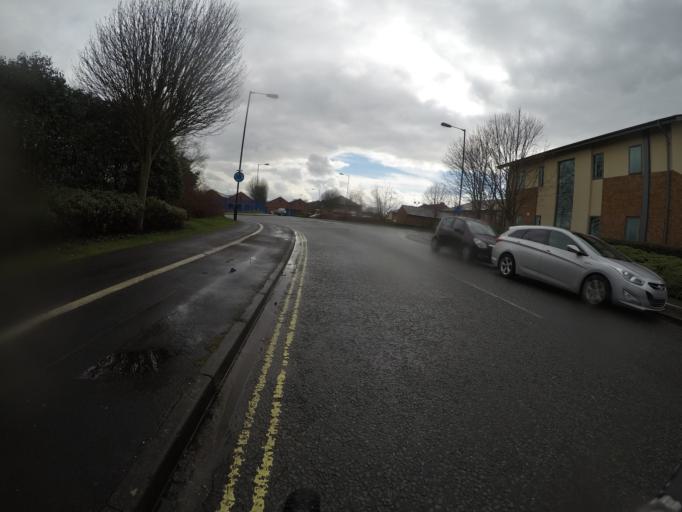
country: GB
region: England
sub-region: City of York
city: York
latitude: 53.9581
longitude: -1.1086
